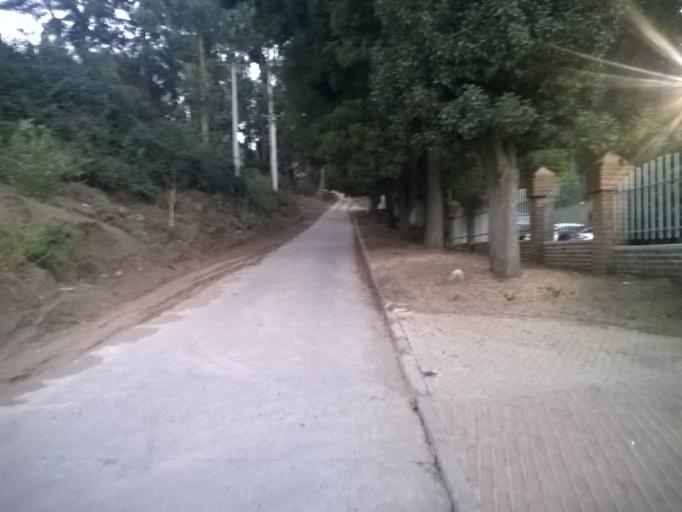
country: CL
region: Valparaiso
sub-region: Provincia de Valparaiso
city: Vina del Mar
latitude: -32.9657
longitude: -71.5299
